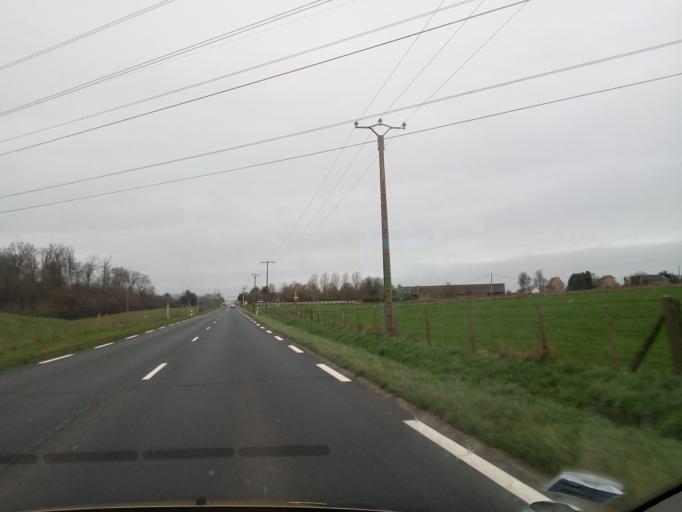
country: FR
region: Haute-Normandie
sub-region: Departement de l'Eure
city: Bourg-Achard
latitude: 49.3792
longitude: 0.8042
